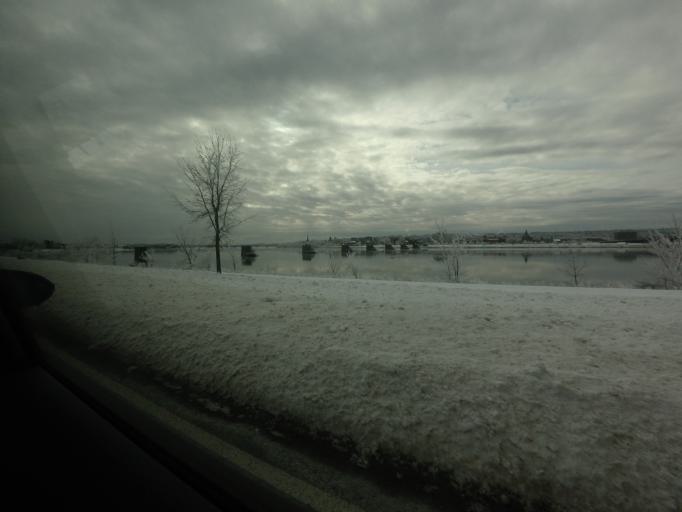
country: CA
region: New Brunswick
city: Fredericton
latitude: 45.9700
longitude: -66.6368
